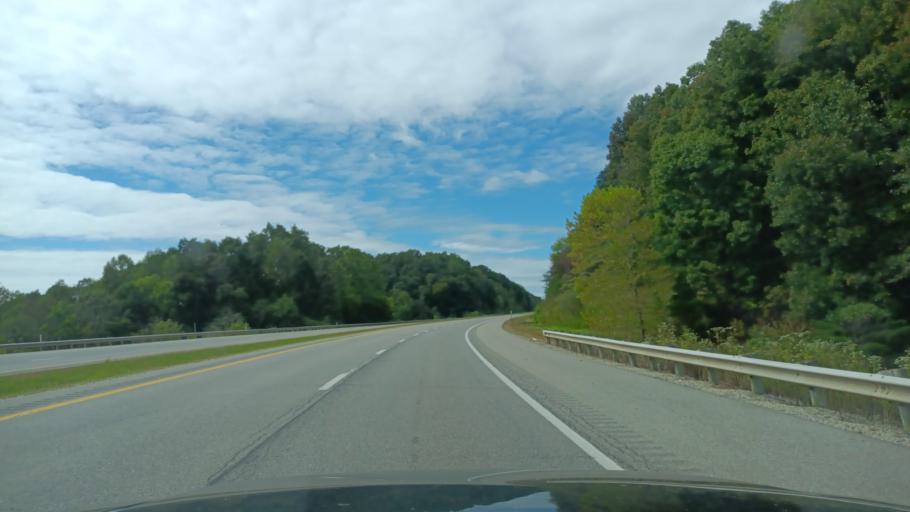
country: US
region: West Virginia
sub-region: Ritchie County
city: Pennsboro
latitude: 39.2648
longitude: -80.9265
